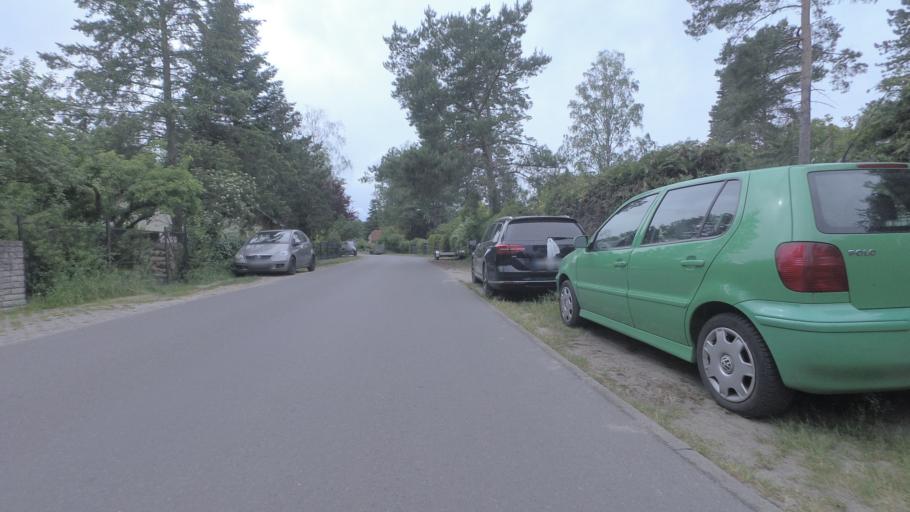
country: DE
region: Brandenburg
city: Bestensee
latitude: 52.2723
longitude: 13.7491
